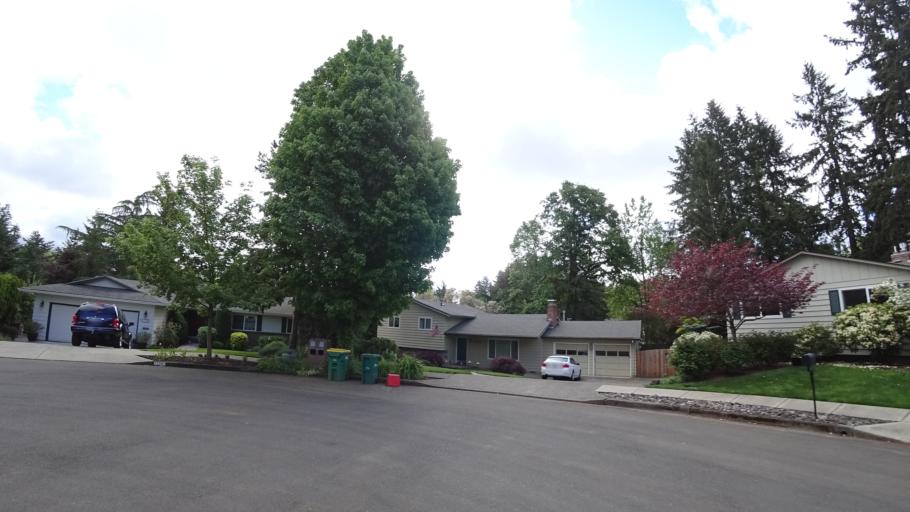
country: US
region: Oregon
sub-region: Washington County
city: Beaverton
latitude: 45.4684
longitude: -122.8210
